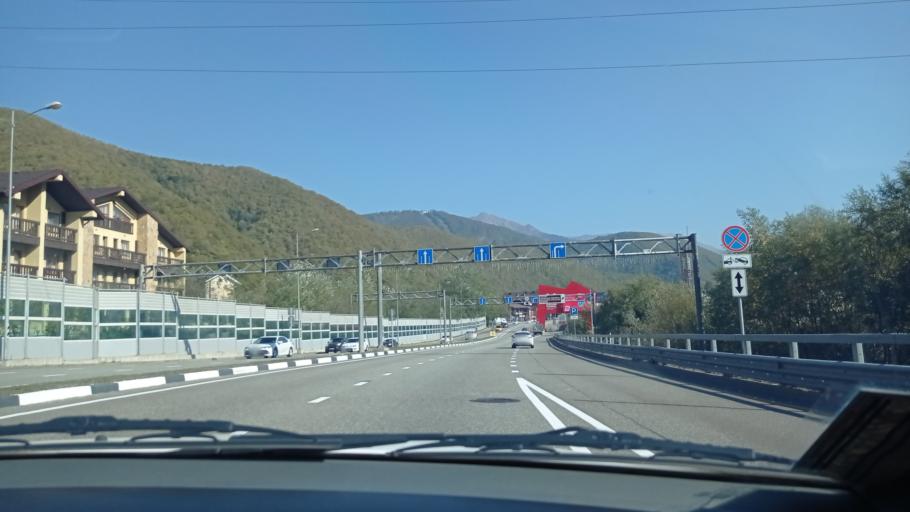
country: RU
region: Krasnodarskiy
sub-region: Sochi City
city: Krasnaya Polyana
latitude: 43.6867
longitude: 40.2460
